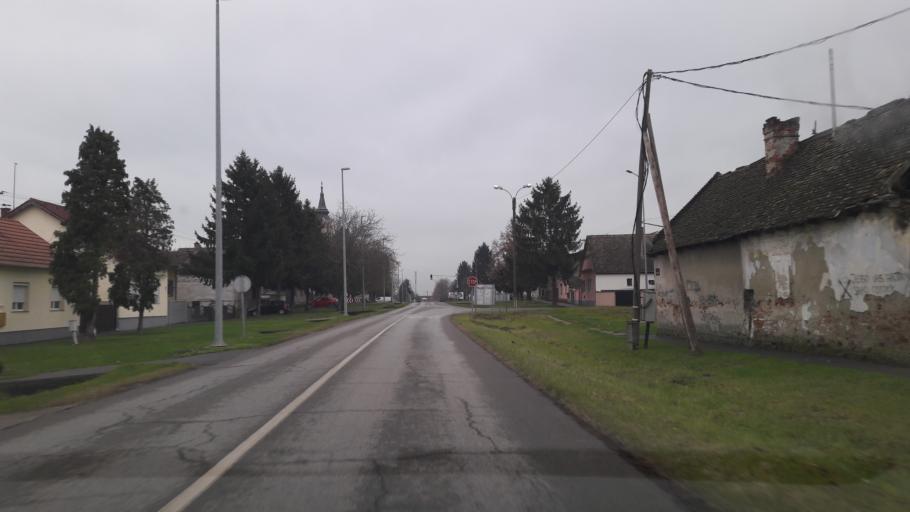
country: HR
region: Osjecko-Baranjska
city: Josipovac
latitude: 45.5831
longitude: 18.5817
